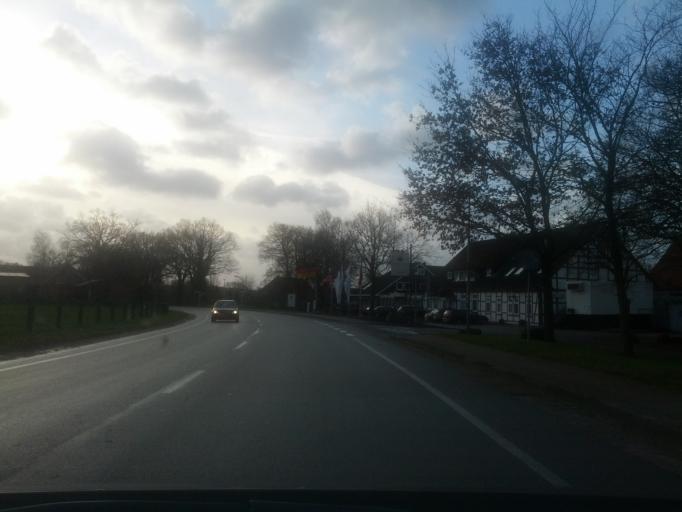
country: DE
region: Lower Saxony
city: Hamersen
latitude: 53.2545
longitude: 9.4819
